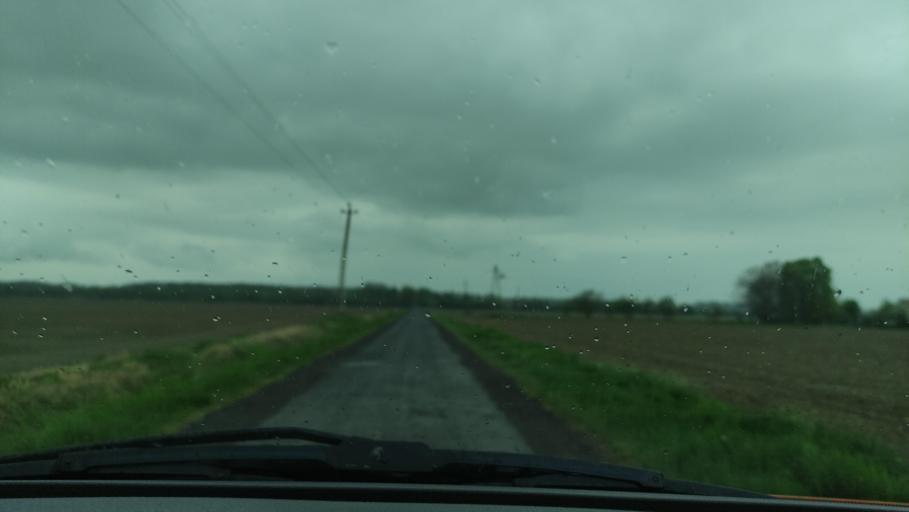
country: HR
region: Osjecko-Baranjska
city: Batina
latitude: 45.9027
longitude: 18.7723
